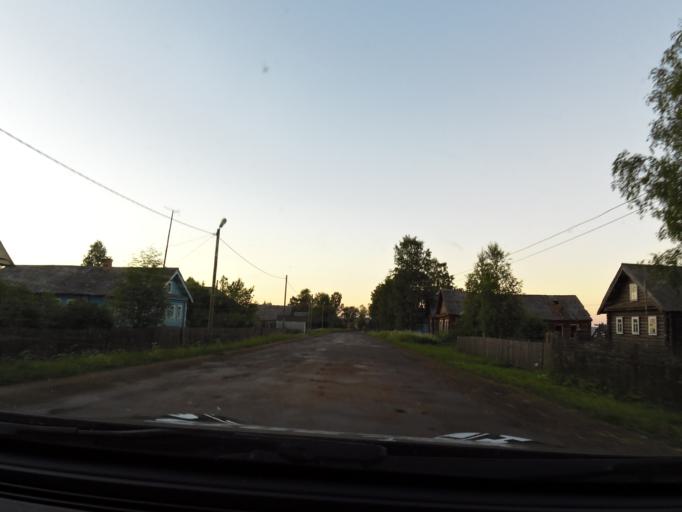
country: RU
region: Leningrad
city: Voznesen'ye
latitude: 60.8310
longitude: 35.7460
